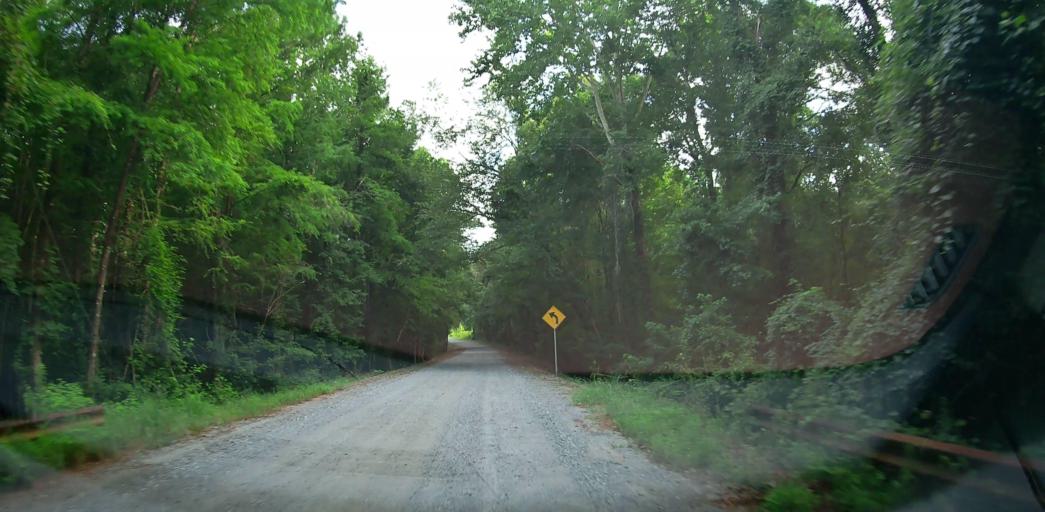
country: US
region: Georgia
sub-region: Bleckley County
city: Cochran
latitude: 32.4275
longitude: -83.4541
